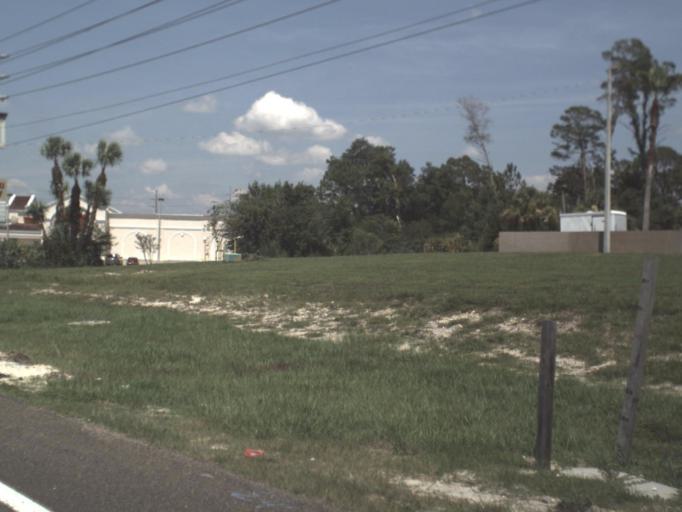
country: US
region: Florida
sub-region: Hernando County
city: North Weeki Wachee
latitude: 28.5171
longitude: -82.5723
